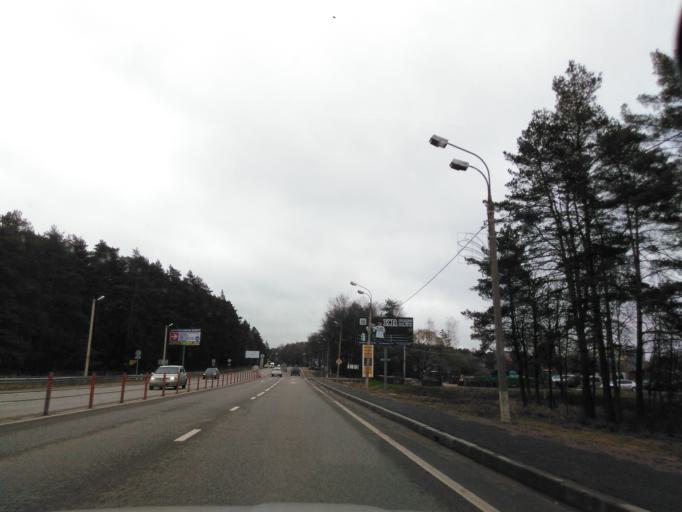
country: RU
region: Moskovskaya
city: Nakhabino
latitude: 55.8432
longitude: 37.2072
